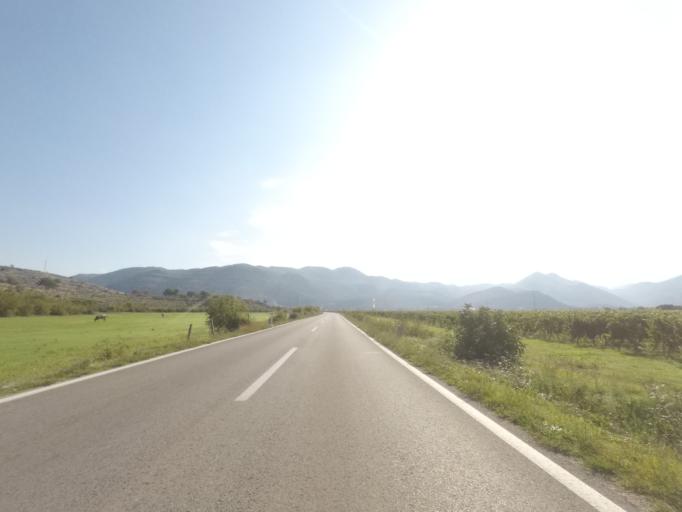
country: BA
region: Republika Srpska
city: Trebinje
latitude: 42.6858
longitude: 18.3171
